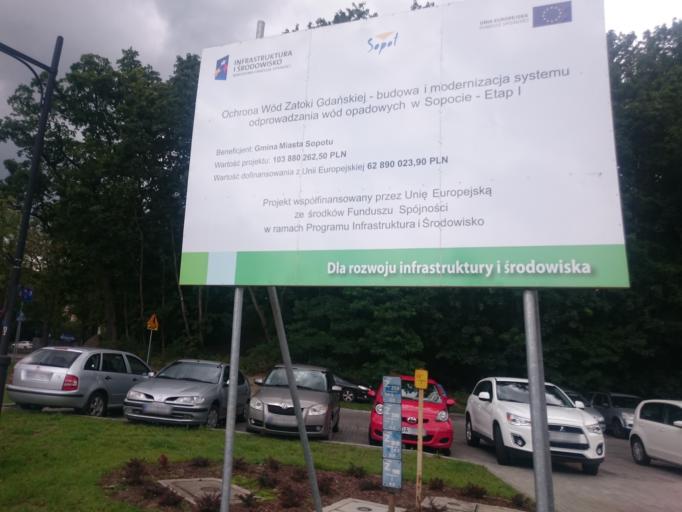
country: PL
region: Pomeranian Voivodeship
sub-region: Sopot
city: Sopot
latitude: 54.4457
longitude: 18.5559
